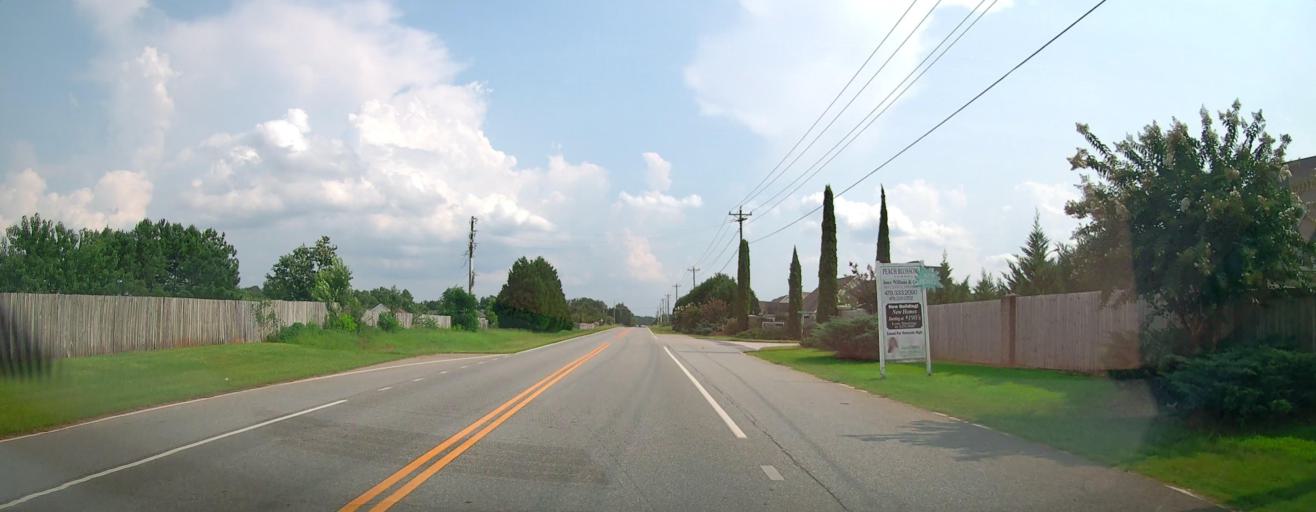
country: US
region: Georgia
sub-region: Houston County
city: Centerville
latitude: 32.5674
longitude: -83.6523
